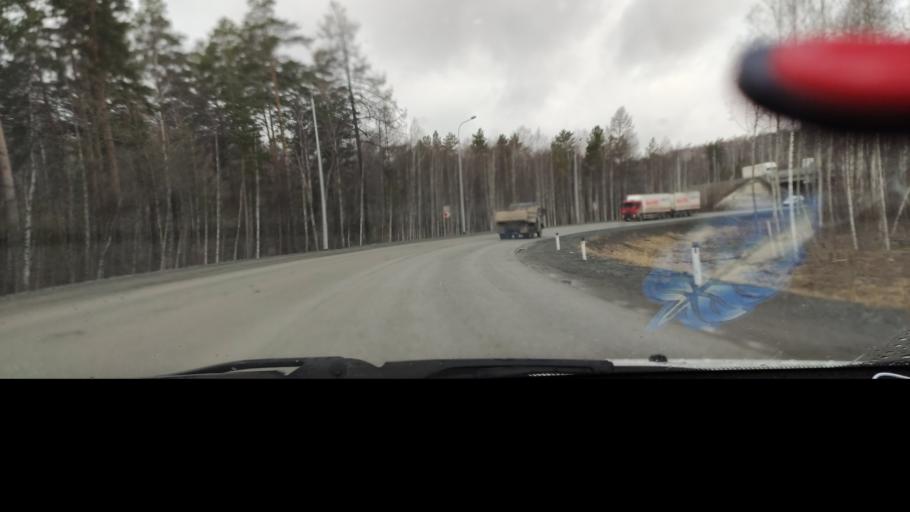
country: RU
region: Sverdlovsk
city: Talitsa
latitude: 56.8513
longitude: 60.0590
